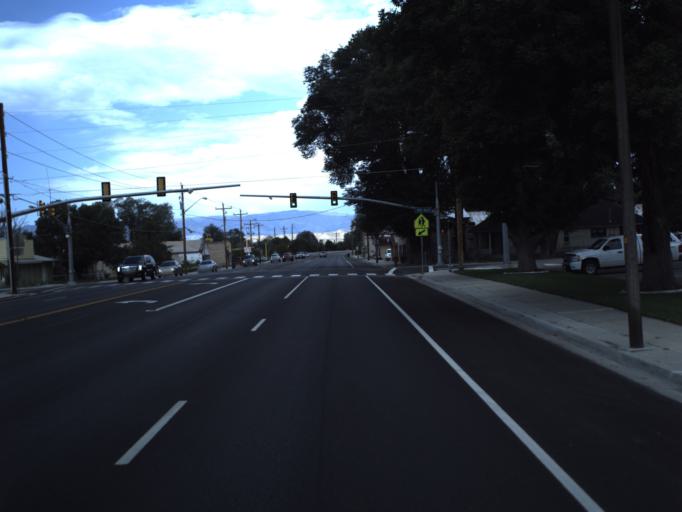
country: US
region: Utah
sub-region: Carbon County
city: Wellington
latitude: 39.5425
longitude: -110.7333
